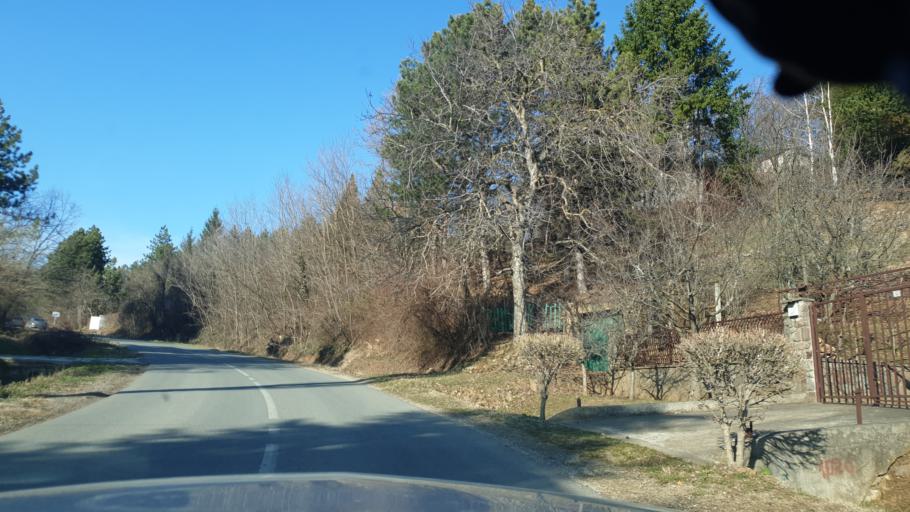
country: RS
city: Vrdnik
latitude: 45.1167
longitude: 19.7746
